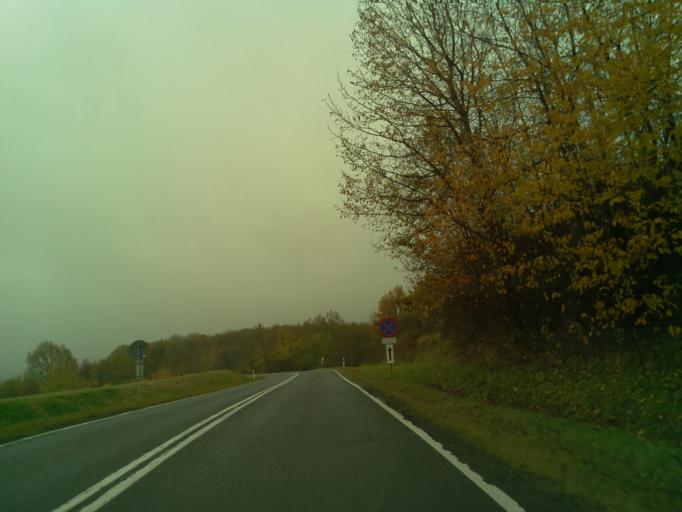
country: PL
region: Lower Silesian Voivodeship
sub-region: Powiat walbrzyski
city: Stare Bogaczowice
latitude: 50.9001
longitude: 16.2563
